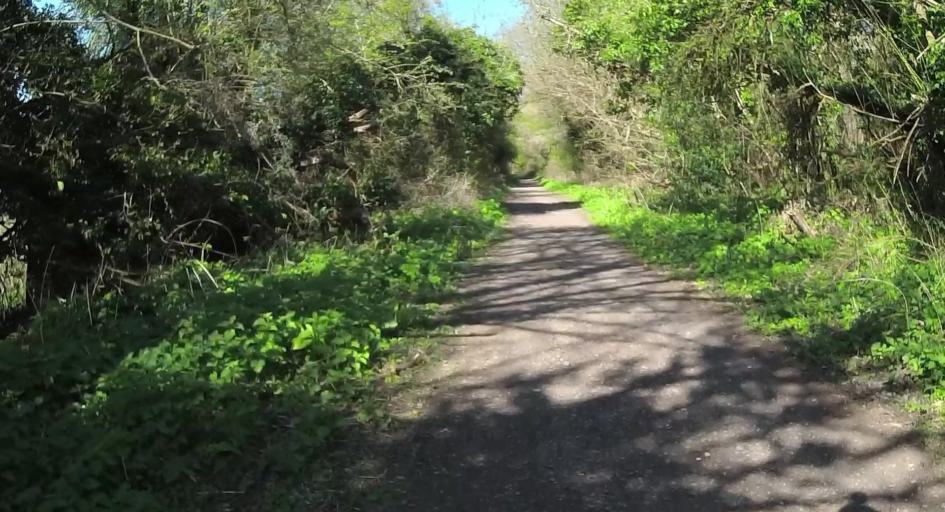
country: GB
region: England
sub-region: Hampshire
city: Romsey
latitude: 51.0914
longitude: -1.4988
